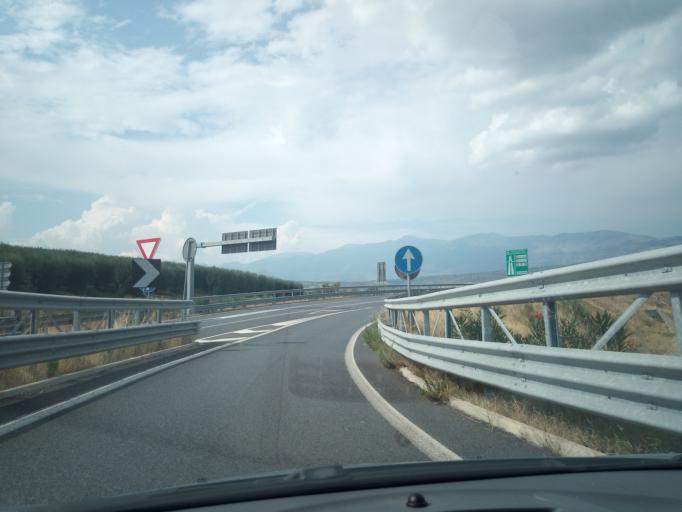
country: IT
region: Calabria
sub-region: Provincia di Cosenza
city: Firmo
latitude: 39.7217
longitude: 16.2366
